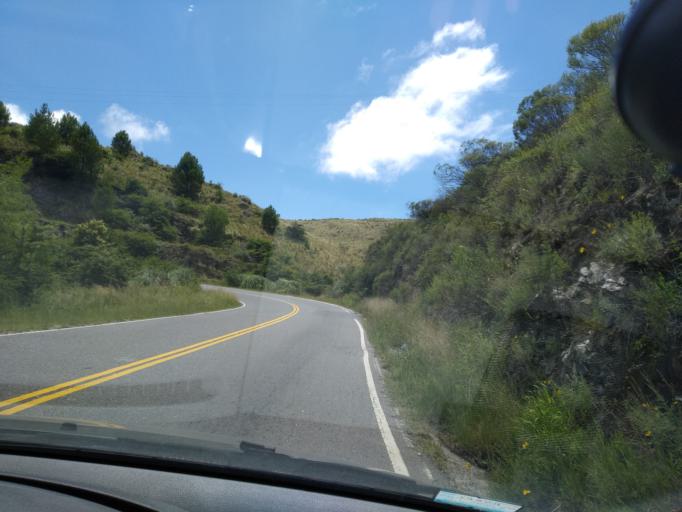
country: AR
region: Cordoba
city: Cuesta Blanca
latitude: -31.6019
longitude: -64.5440
